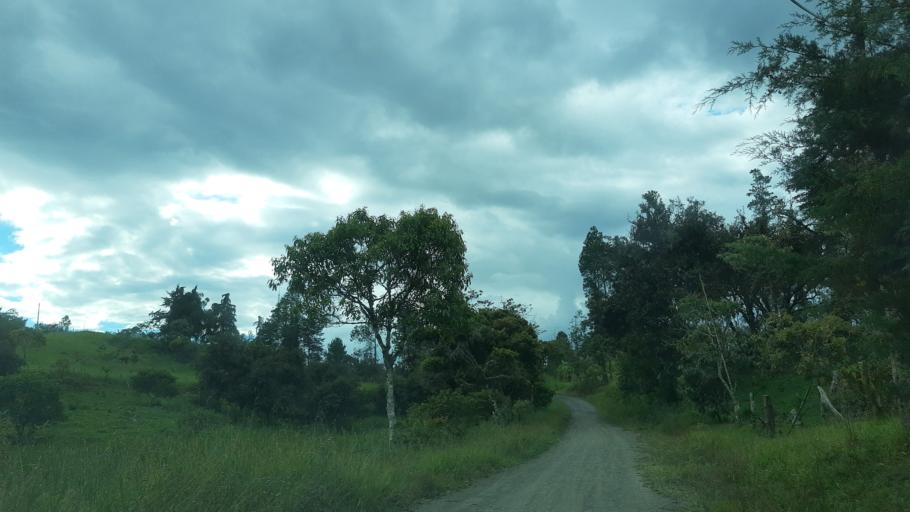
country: CO
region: Boyaca
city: Garagoa
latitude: 5.0201
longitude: -73.3309
